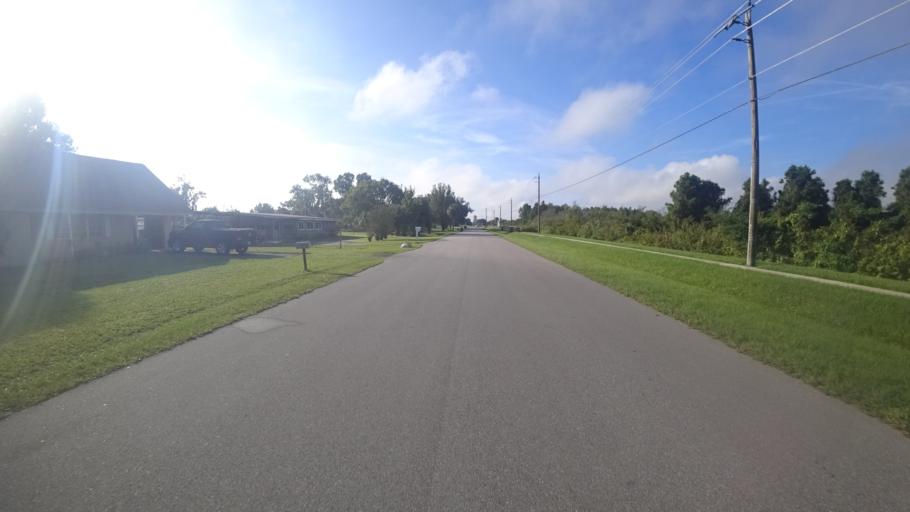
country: US
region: Florida
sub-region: Manatee County
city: Ellenton
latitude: 27.5506
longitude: -82.4664
